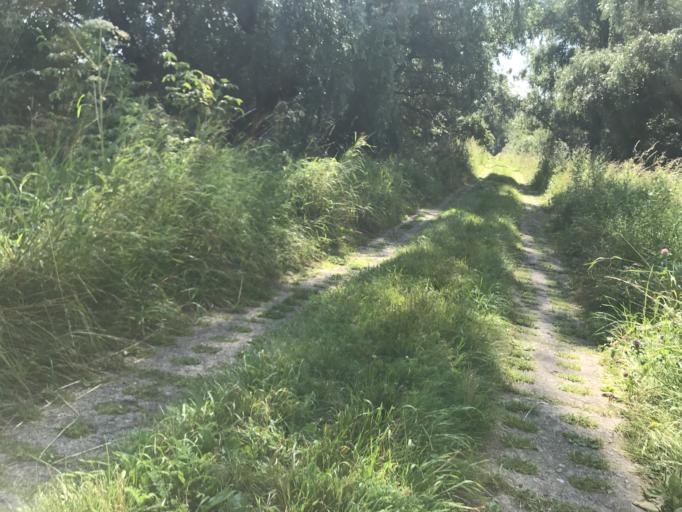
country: PL
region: Pomeranian Voivodeship
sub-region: Gdansk
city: Gdansk
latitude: 54.3196
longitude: 18.6732
